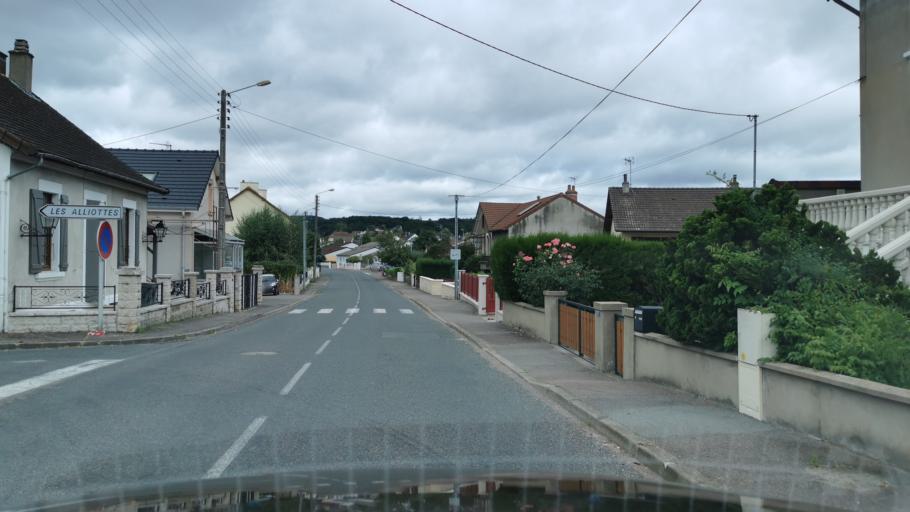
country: FR
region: Bourgogne
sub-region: Departement de Saone-et-Loire
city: Le Breuil
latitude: 46.8024
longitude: 4.4725
